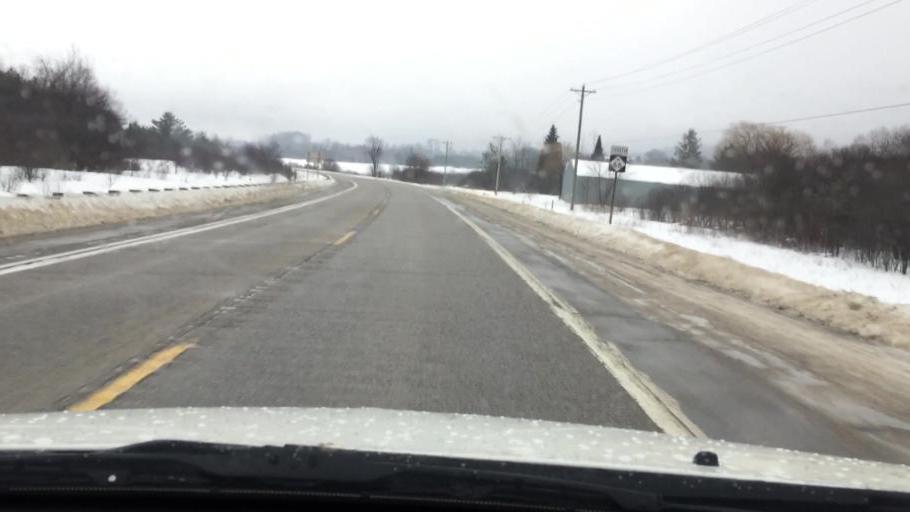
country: US
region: Michigan
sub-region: Charlevoix County
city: East Jordan
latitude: 45.1317
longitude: -85.1393
